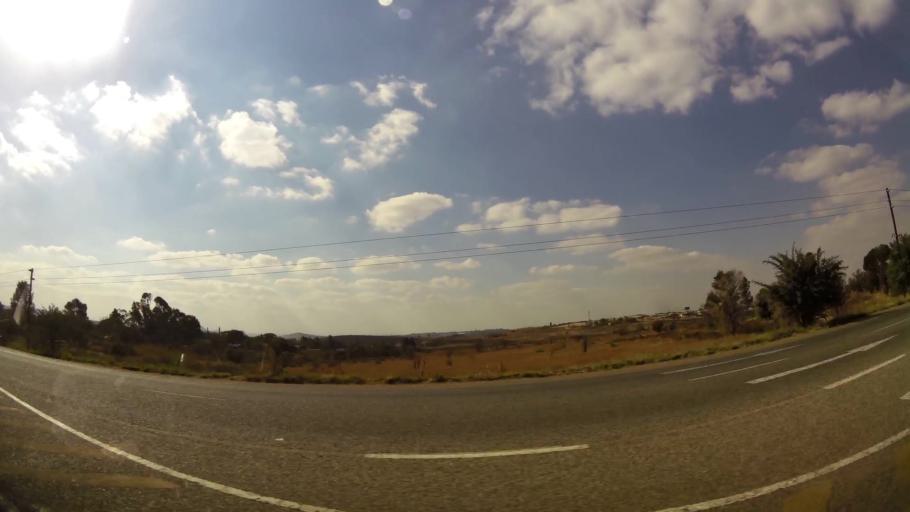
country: ZA
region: Gauteng
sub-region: West Rand District Municipality
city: Muldersdriseloop
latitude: -26.0585
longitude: 27.8268
